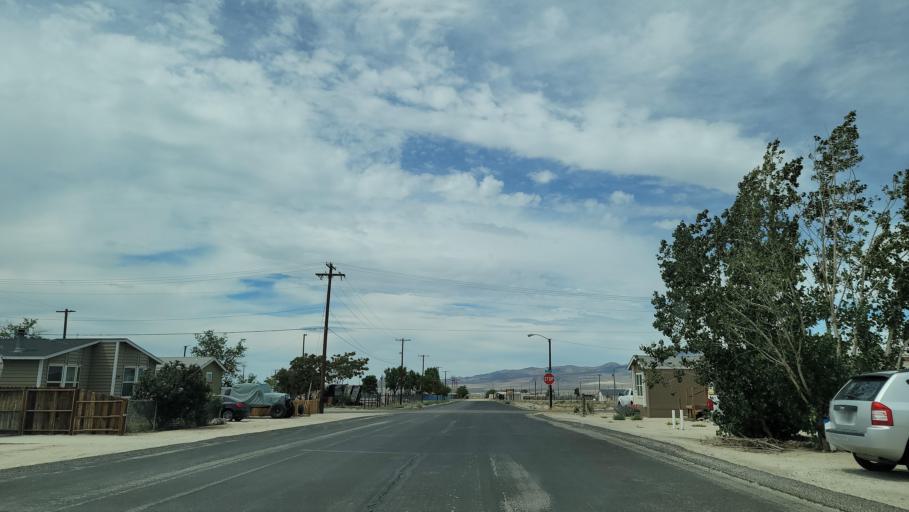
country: US
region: Nevada
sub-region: Mineral County
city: Hawthorne
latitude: 38.5270
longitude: -118.6161
